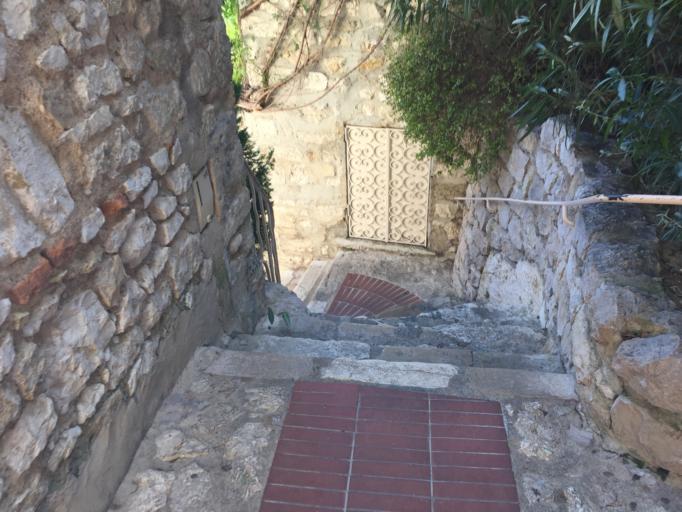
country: FR
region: Provence-Alpes-Cote d'Azur
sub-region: Departement des Alpes-Maritimes
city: Eze
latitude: 43.7274
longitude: 7.3619
